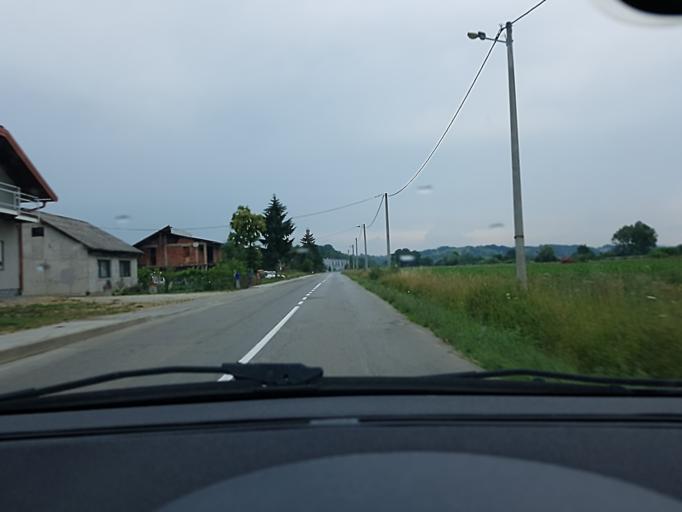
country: HR
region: Zagrebacka
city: Pojatno
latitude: 45.9374
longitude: 15.8130
